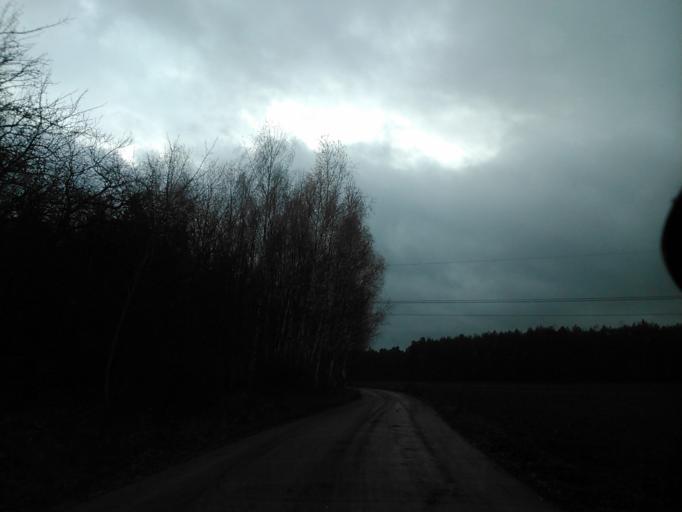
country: PL
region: Kujawsko-Pomorskie
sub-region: Powiat golubsko-dobrzynski
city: Golub-Dobrzyn
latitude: 53.1163
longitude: 19.1022
